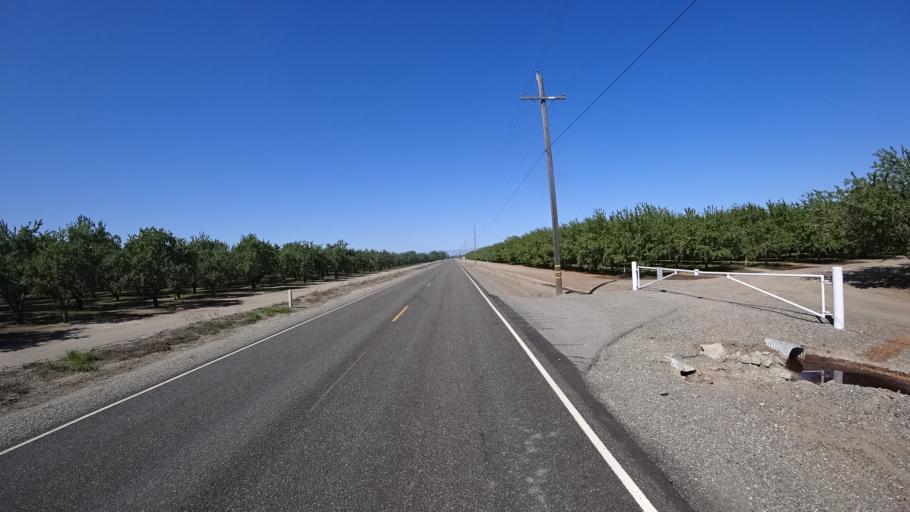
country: US
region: California
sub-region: Glenn County
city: Hamilton City
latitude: 39.7106
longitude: -122.0899
